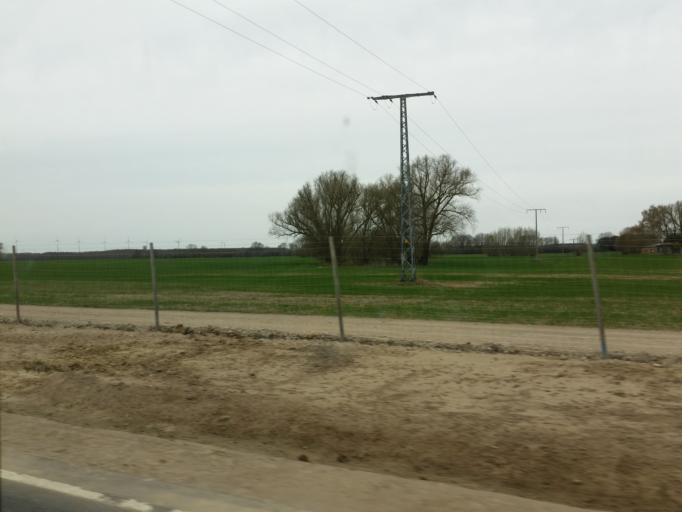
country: DE
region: Mecklenburg-Vorpommern
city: Grimmen
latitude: 54.0981
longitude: 13.1387
